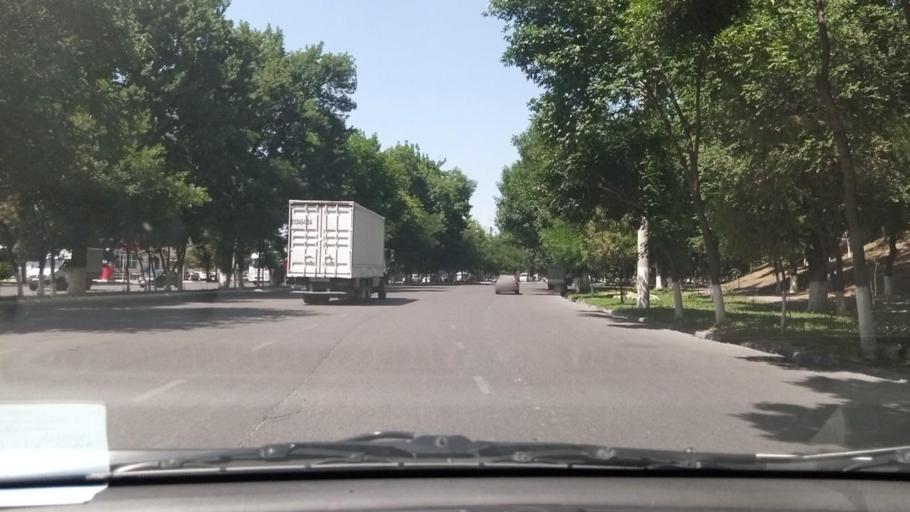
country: UZ
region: Toshkent Shahri
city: Tashkent
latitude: 41.2555
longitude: 69.2155
